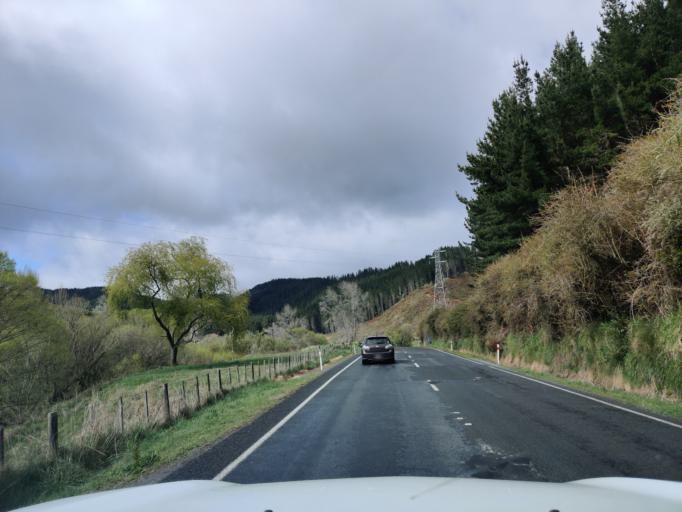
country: NZ
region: Waikato
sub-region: Otorohanga District
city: Otorohanga
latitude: -38.6130
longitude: 175.2189
